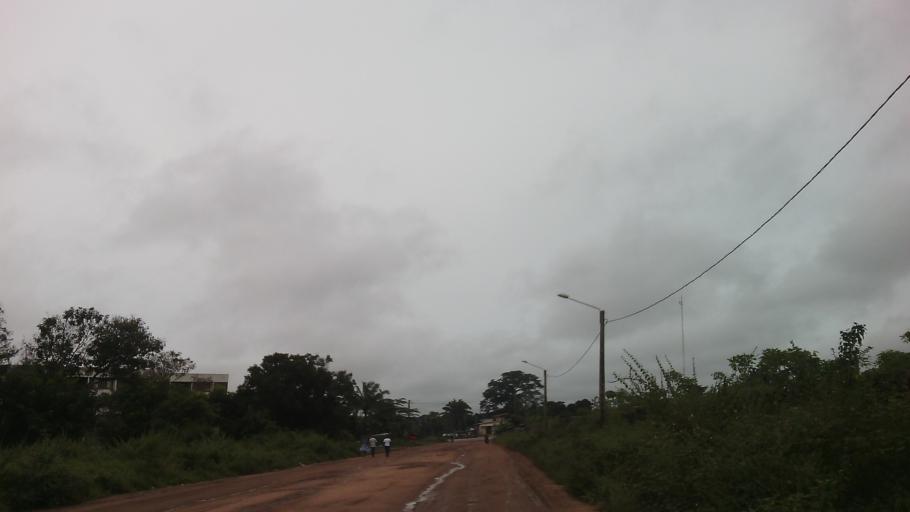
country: CI
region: Vallee du Bandama
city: Bouake
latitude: 7.6890
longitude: -5.0581
